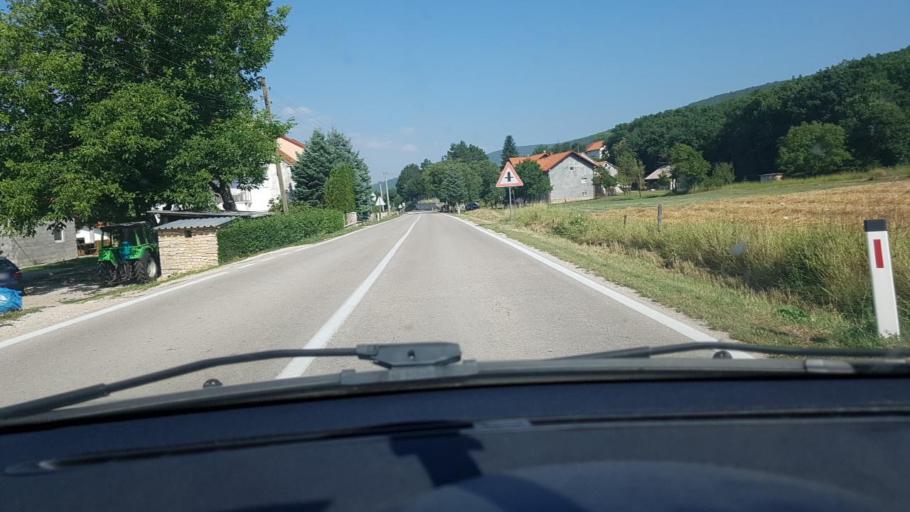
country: BA
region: Federation of Bosnia and Herzegovina
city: Orguz
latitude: 43.8720
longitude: 16.8728
